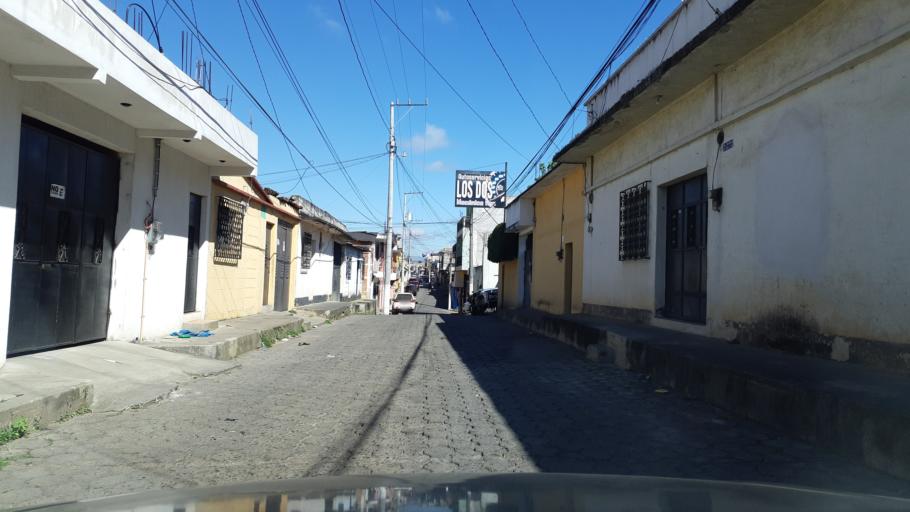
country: GT
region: Chimaltenango
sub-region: Municipio de Chimaltenango
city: Chimaltenango
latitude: 14.6592
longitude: -90.8224
